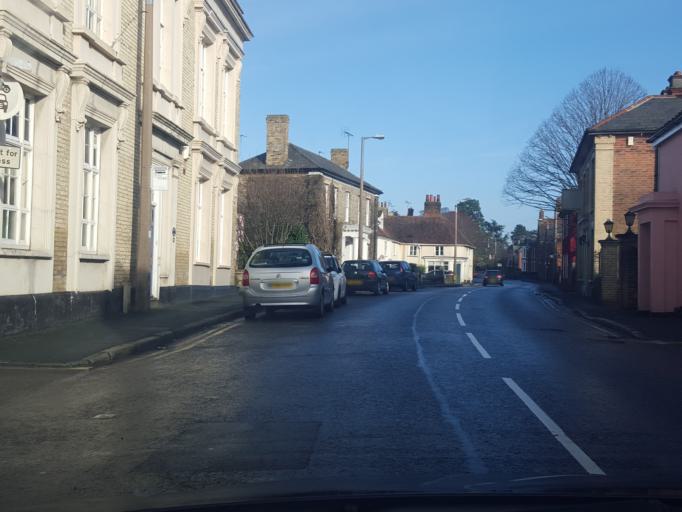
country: GB
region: England
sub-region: Essex
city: Sible Hedingham
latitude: 51.9467
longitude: 0.6417
